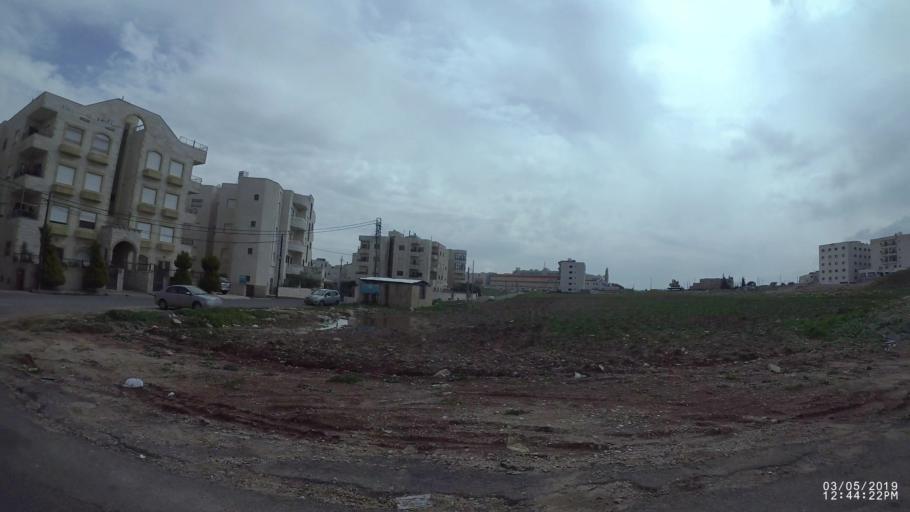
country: JO
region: Amman
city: Amman
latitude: 31.9967
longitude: 35.9337
